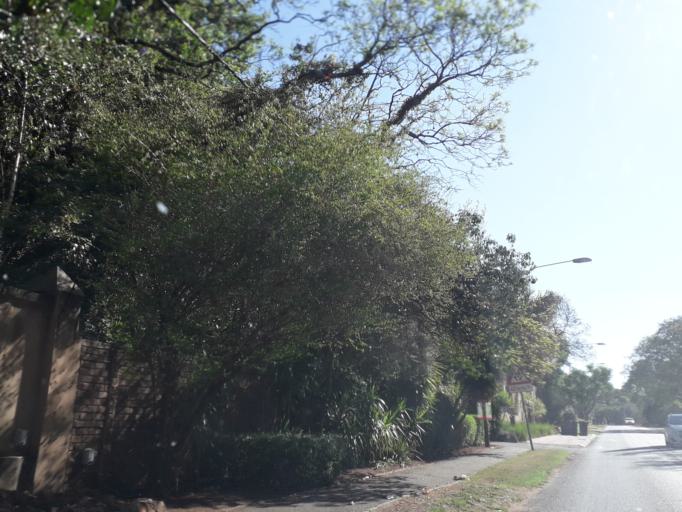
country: ZA
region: Gauteng
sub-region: City of Johannesburg Metropolitan Municipality
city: Johannesburg
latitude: -26.1339
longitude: 27.9716
